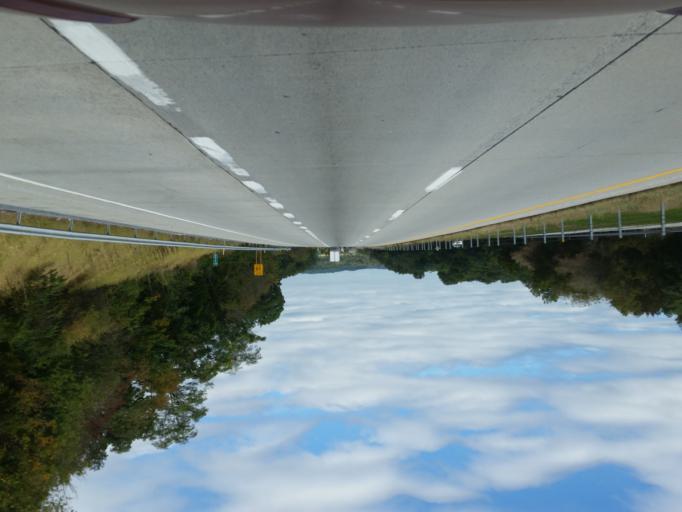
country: US
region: Pennsylvania
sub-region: Lancaster County
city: Elizabethtown
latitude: 40.1745
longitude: -76.5960
